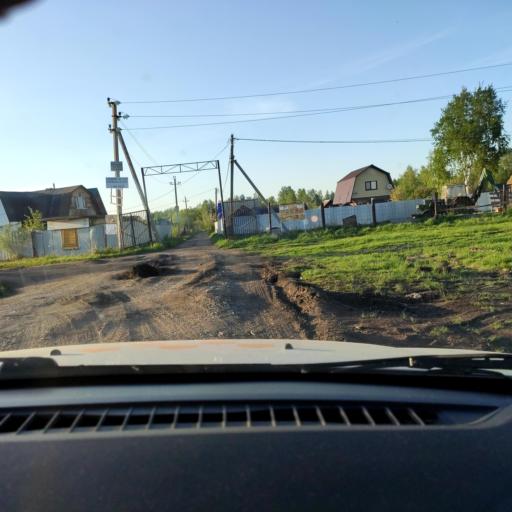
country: RU
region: Bashkortostan
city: Asanovo
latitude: 54.9077
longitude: 55.6179
